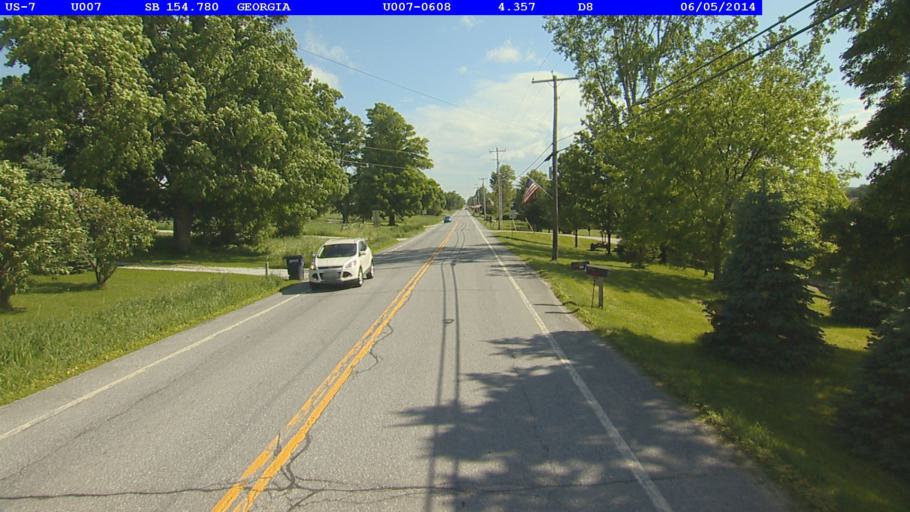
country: US
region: Vermont
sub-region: Franklin County
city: Saint Albans
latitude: 44.7341
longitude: -73.1163
